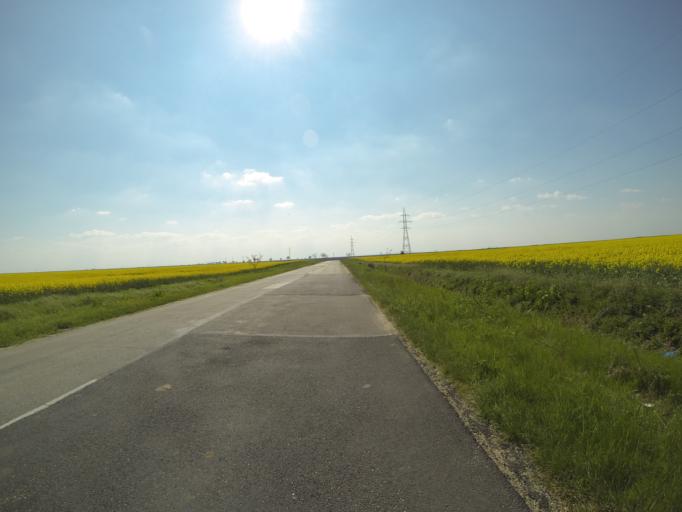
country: RO
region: Mehedinti
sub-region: Comuna Darvari
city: Gemeni
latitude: 44.1475
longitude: 23.1010
